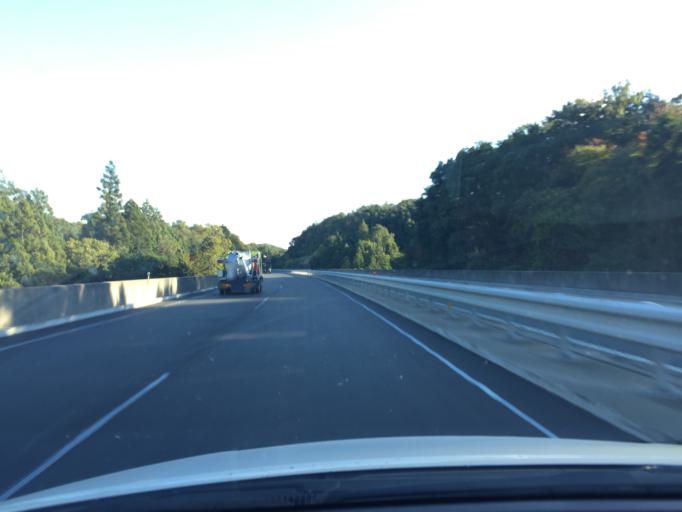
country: JP
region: Fukushima
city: Iwaki
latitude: 37.0594
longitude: 140.7981
